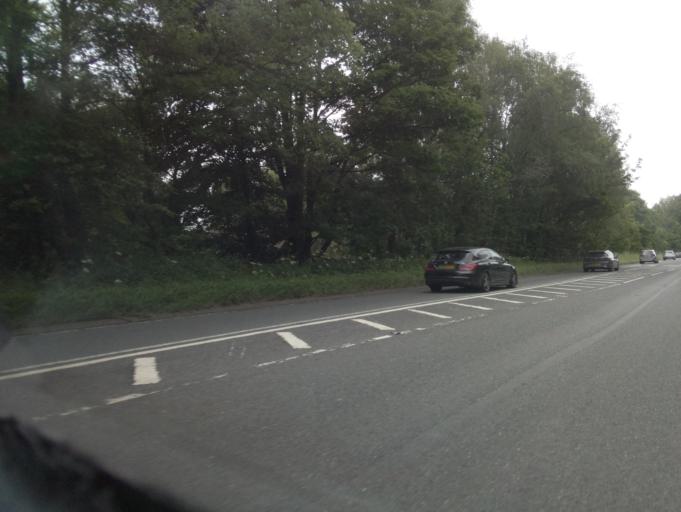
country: GB
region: England
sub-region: Staffordshire
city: Mayfield
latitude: 52.9972
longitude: -1.7501
